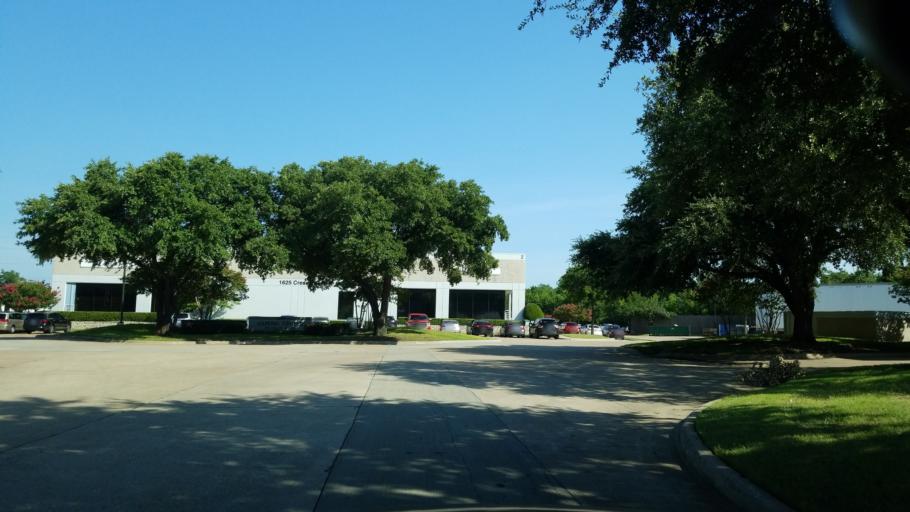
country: US
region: Texas
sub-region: Dallas County
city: Carrollton
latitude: 32.9609
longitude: -96.9184
